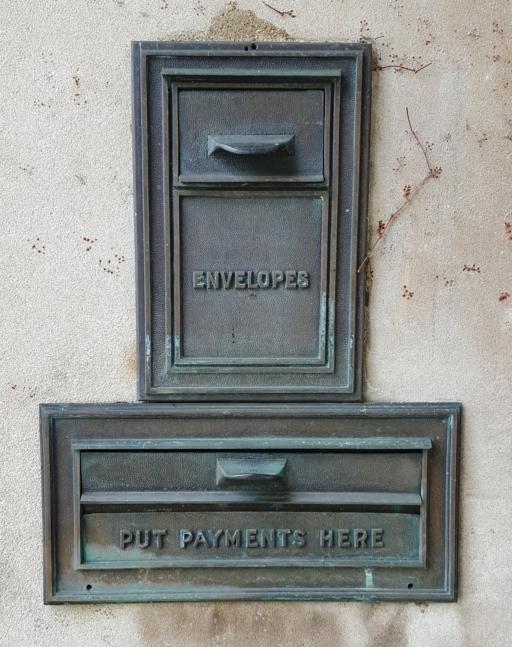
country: US
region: Illinois
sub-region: Cook County
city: Winnetka
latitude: 42.1044
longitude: -87.7341
